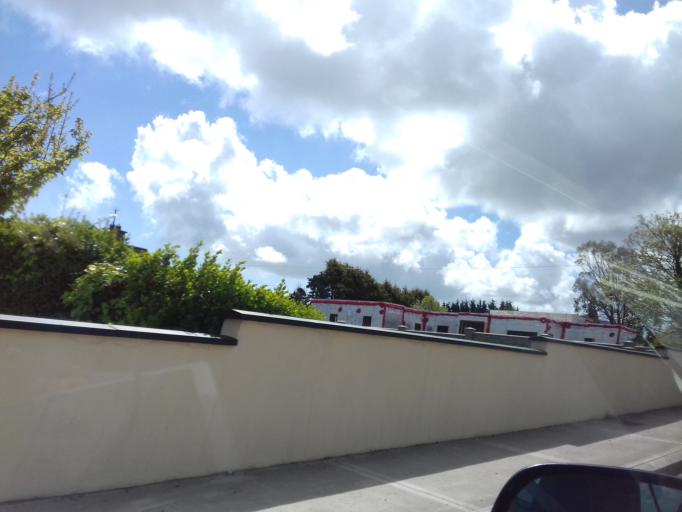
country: IE
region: Leinster
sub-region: Loch Garman
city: Loch Garman
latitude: 52.3569
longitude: -6.4529
